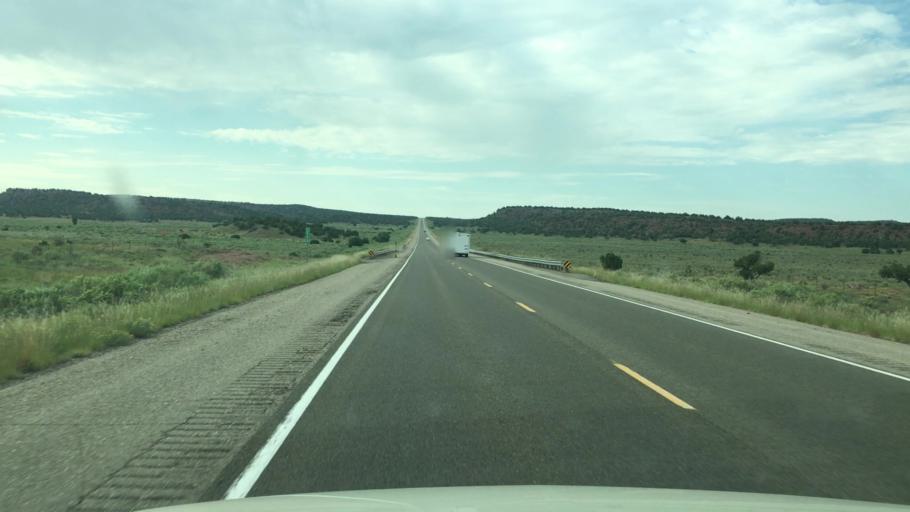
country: US
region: New Mexico
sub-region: Santa Fe County
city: Eldorado at Santa Fe
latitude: 35.2507
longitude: -105.8076
